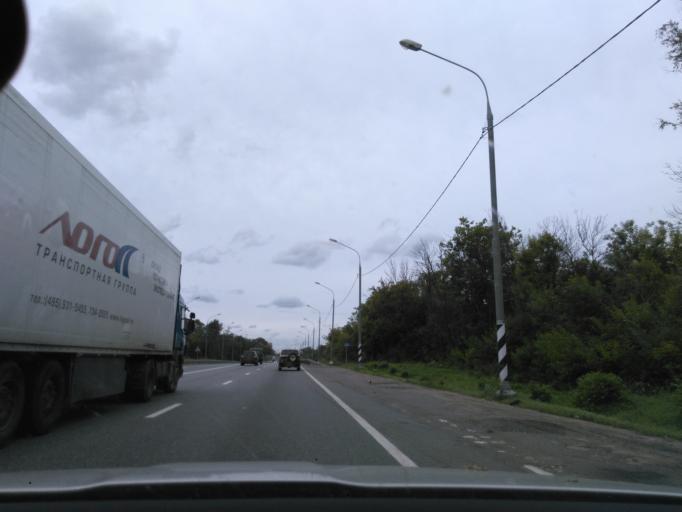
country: RU
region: Moskovskaya
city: Klin
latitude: 56.3115
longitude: 36.7772
